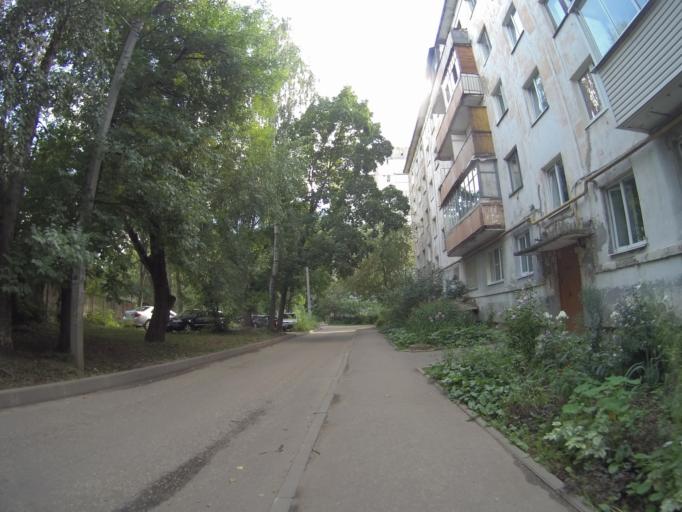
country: RU
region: Vladimir
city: Vladimir
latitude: 56.1338
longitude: 40.3606
